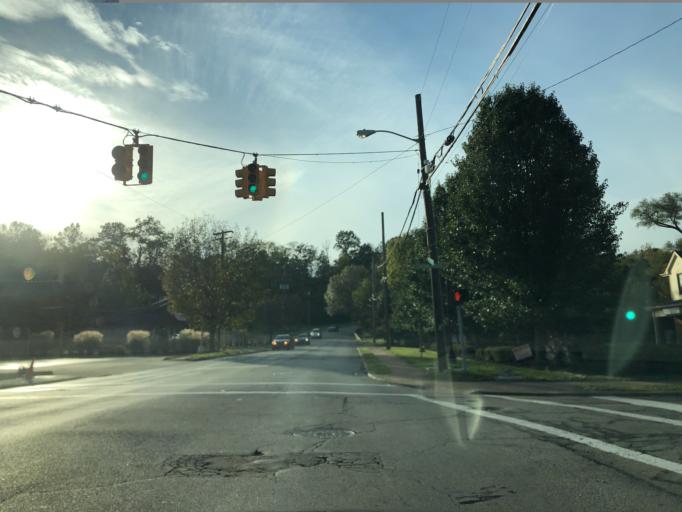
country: US
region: Ohio
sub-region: Hamilton County
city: Loveland
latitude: 39.2691
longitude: -84.2654
